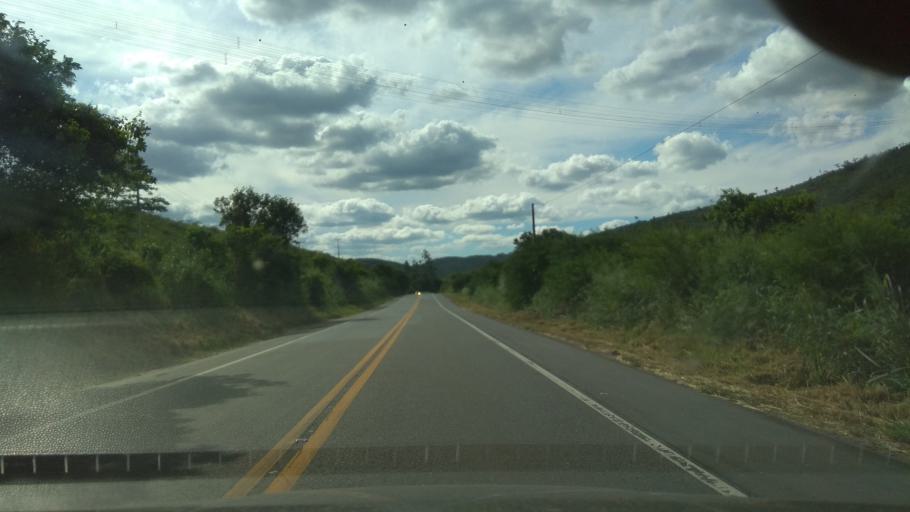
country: BR
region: Bahia
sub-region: Jequie
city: Jequie
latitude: -13.9063
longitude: -40.0177
